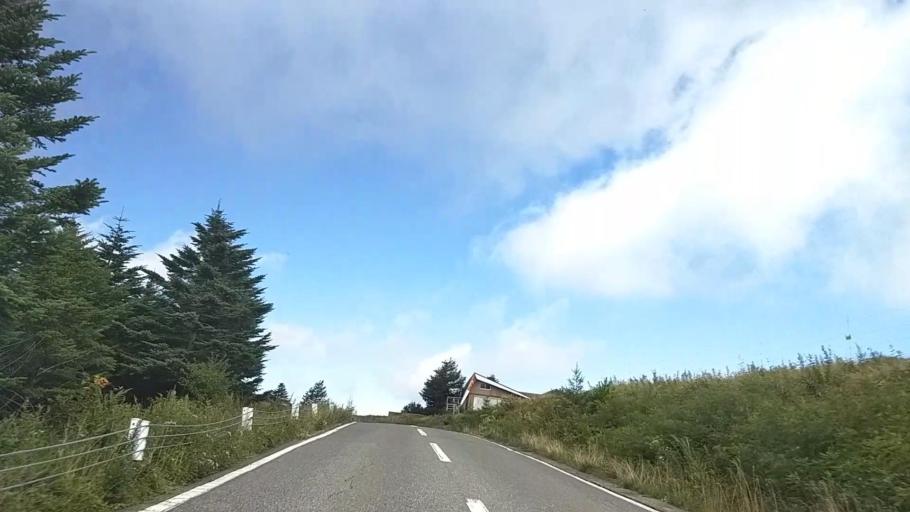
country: JP
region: Nagano
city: Suwa
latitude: 36.1030
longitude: 138.1887
